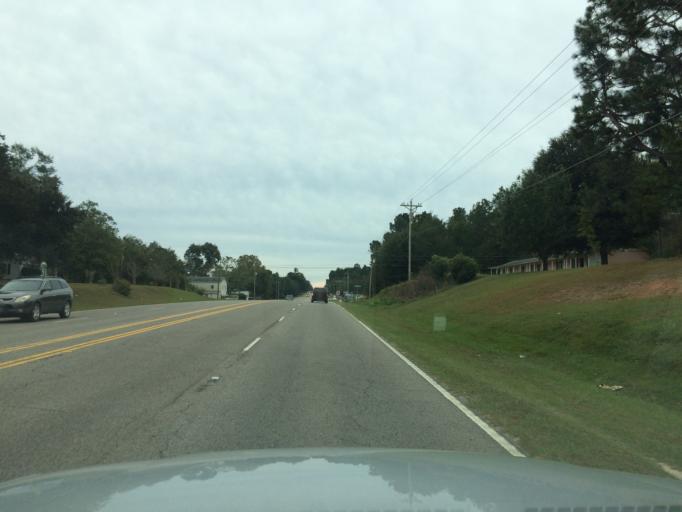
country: US
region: South Carolina
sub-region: Aiken County
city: New Ellenton
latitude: 33.4491
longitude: -81.6867
